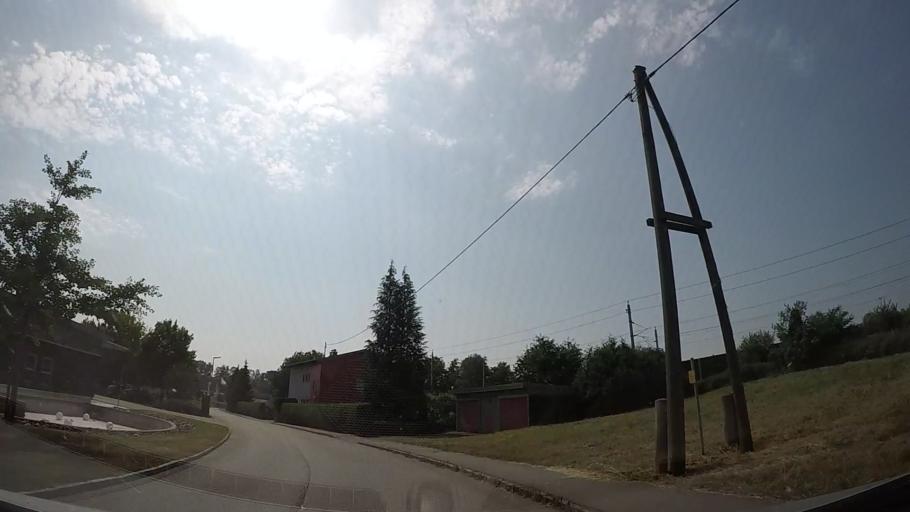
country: AT
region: Upper Austria
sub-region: Politischer Bezirk Grieskirchen
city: Bad Schallerbach
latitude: 48.2272
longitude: 13.9342
